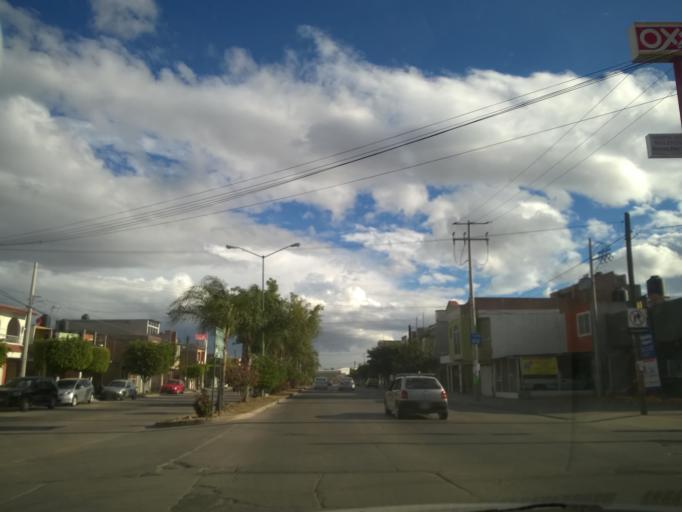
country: MX
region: Guanajuato
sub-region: Leon
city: San Jose de Duran (Los Troncoso)
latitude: 21.0796
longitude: -101.6391
